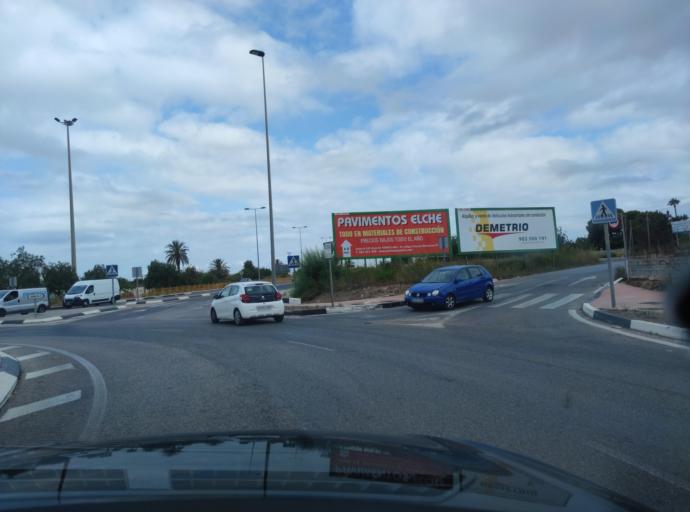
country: ES
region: Valencia
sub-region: Provincia de Alicante
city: Santa Pola
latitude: 38.2020
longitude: -0.5729
